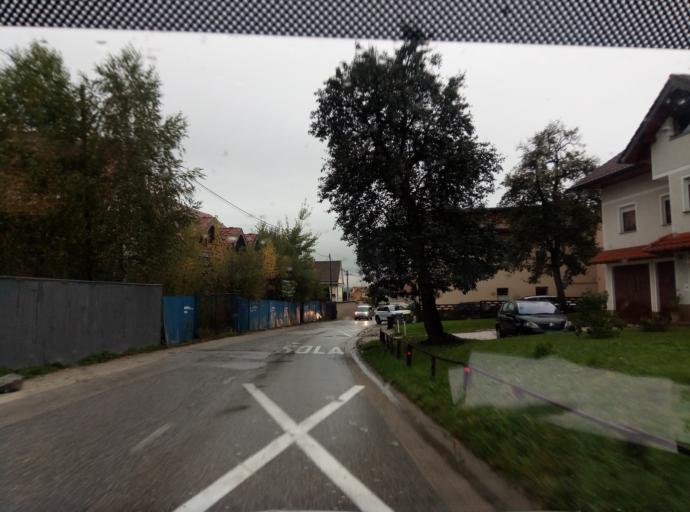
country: SI
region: Medvode
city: Zgornje Pirnice
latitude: 46.1254
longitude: 14.4766
